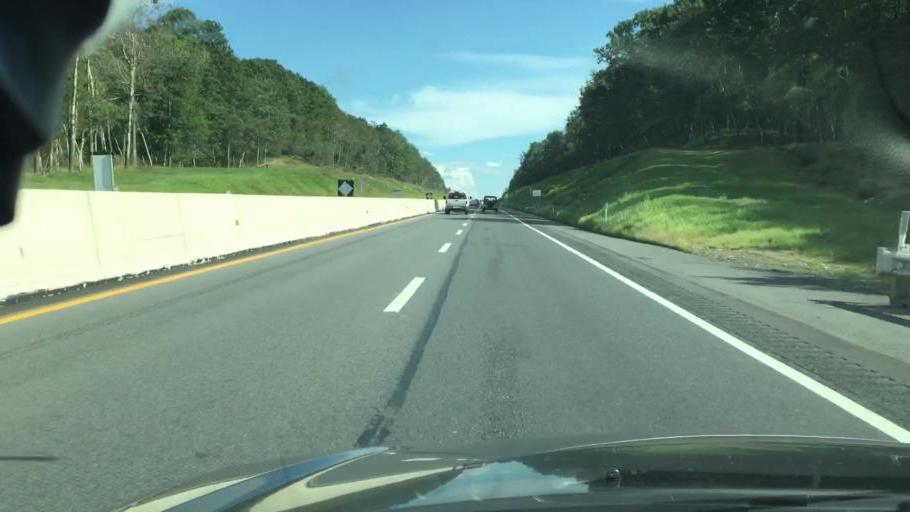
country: US
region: Pennsylvania
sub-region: Luzerne County
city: White Haven
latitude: 41.0662
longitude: -75.6916
